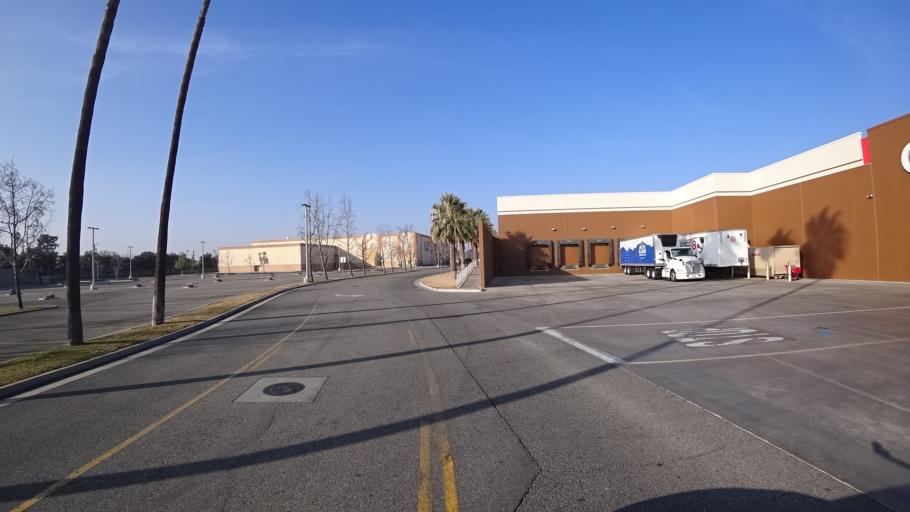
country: US
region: California
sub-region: Kern County
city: Bakersfield
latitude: 35.3360
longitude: -119.0350
